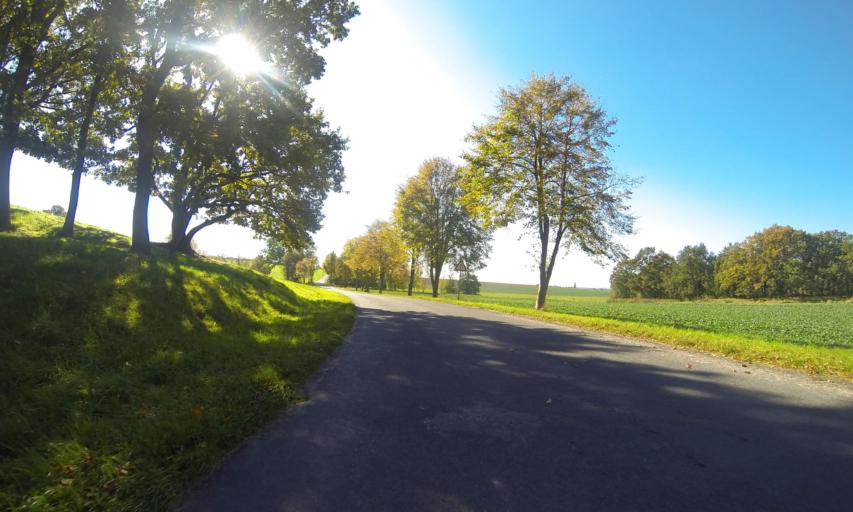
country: DE
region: Saxony
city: Grossenhain
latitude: 51.2562
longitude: 13.5857
